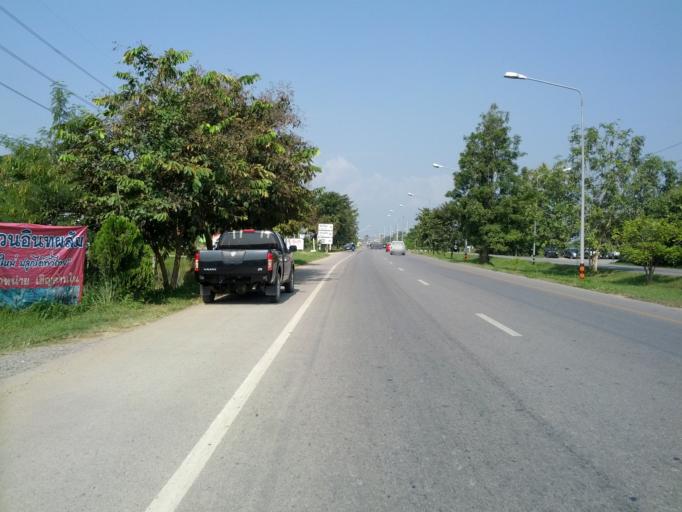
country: TH
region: Chiang Mai
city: Saraphi
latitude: 18.7489
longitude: 99.0659
